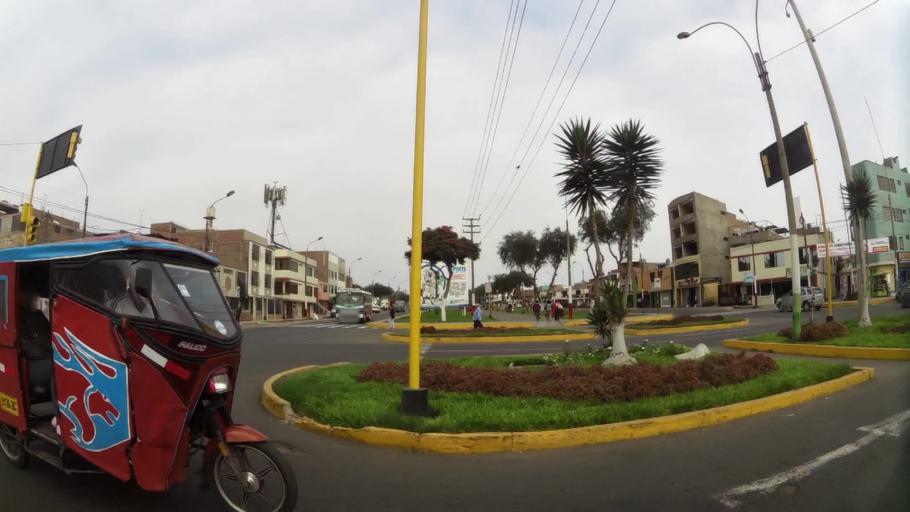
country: PE
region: Callao
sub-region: Callao
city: Callao
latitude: -12.0168
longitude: -77.0928
